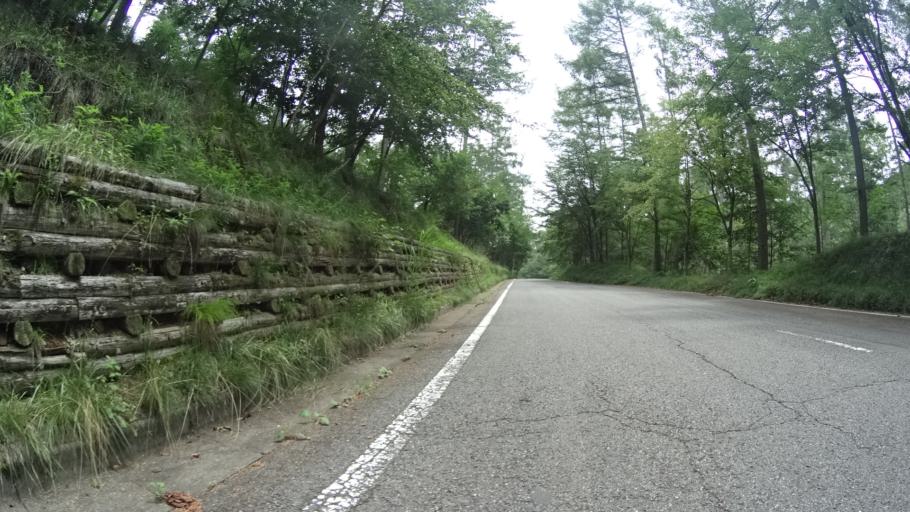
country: JP
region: Yamanashi
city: Nirasaki
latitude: 35.8868
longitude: 138.5702
